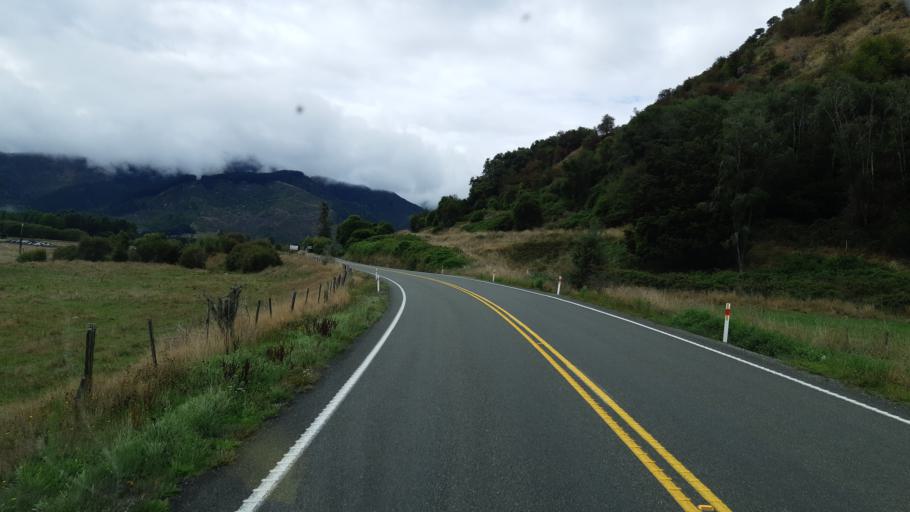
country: NZ
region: West Coast
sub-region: Buller District
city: Westport
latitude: -41.7965
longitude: 172.3100
